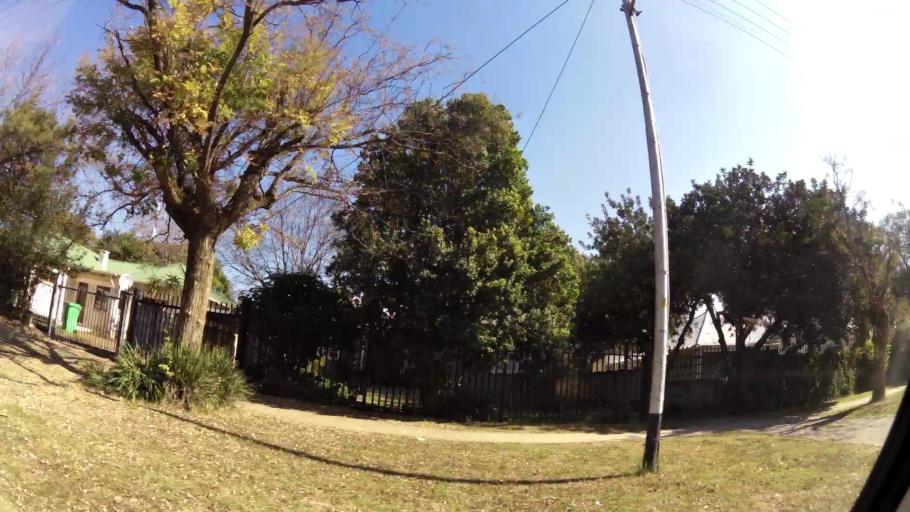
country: ZA
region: Gauteng
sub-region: City of Tshwane Metropolitan Municipality
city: Pretoria
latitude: -25.7537
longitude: 28.2452
